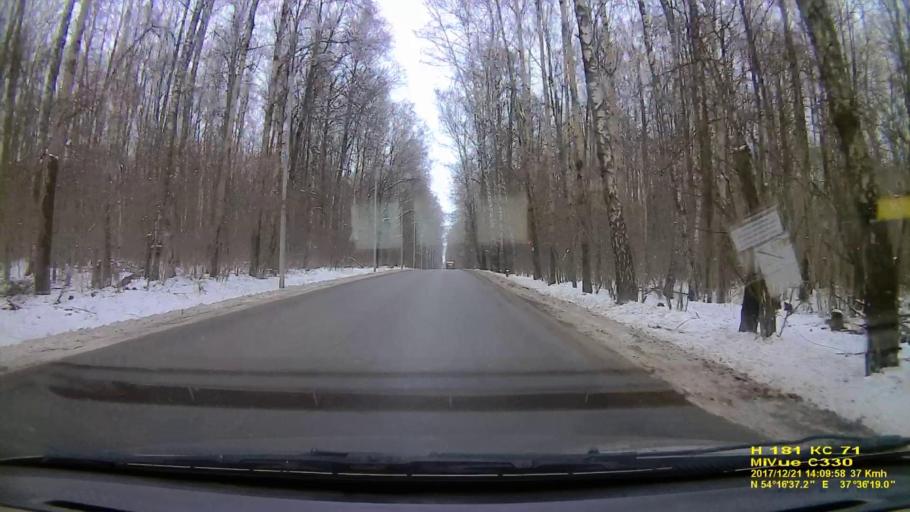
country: RU
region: Tula
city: Gorelki
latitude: 54.2772
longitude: 37.6053
